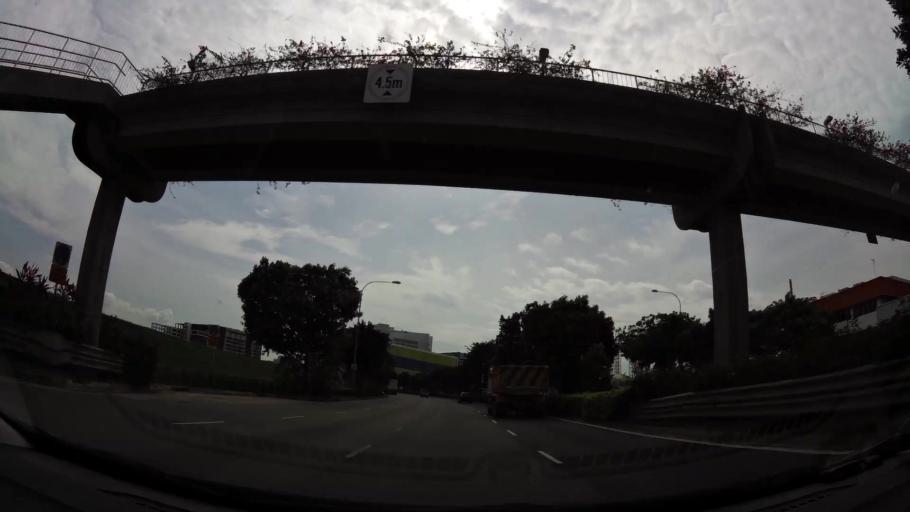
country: SG
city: Singapore
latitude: 1.3041
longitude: 103.7431
